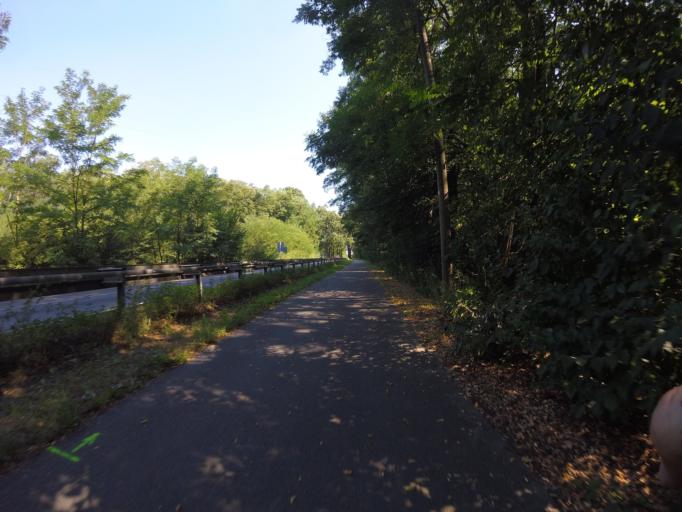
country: DE
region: Brandenburg
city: Mullrose
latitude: 52.2730
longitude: 14.4412
